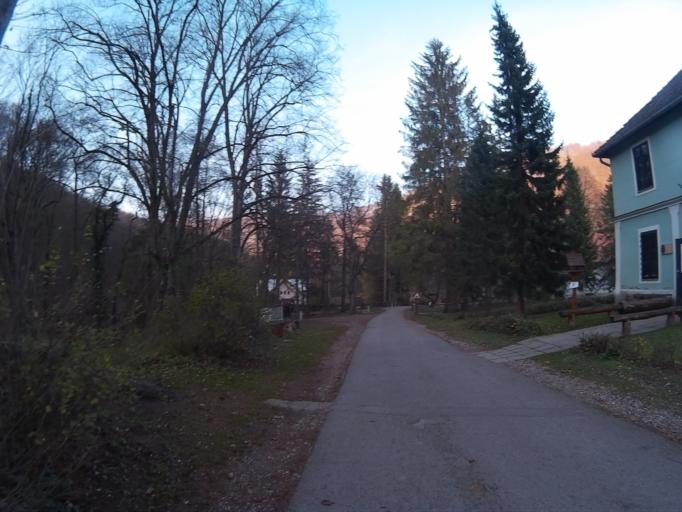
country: HU
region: Heves
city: Szilvasvarad
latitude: 48.0851
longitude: 20.4062
